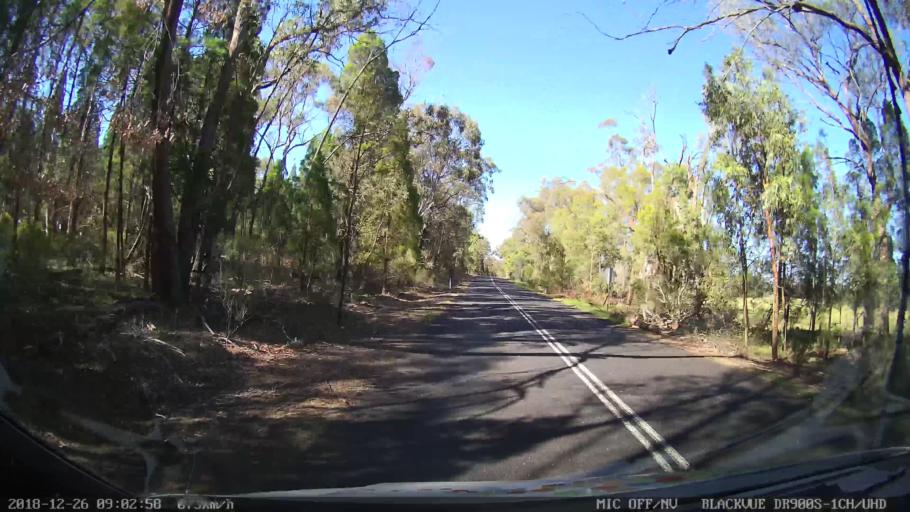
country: AU
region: New South Wales
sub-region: Mid-Western Regional
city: Kandos
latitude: -32.6580
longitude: 150.0161
